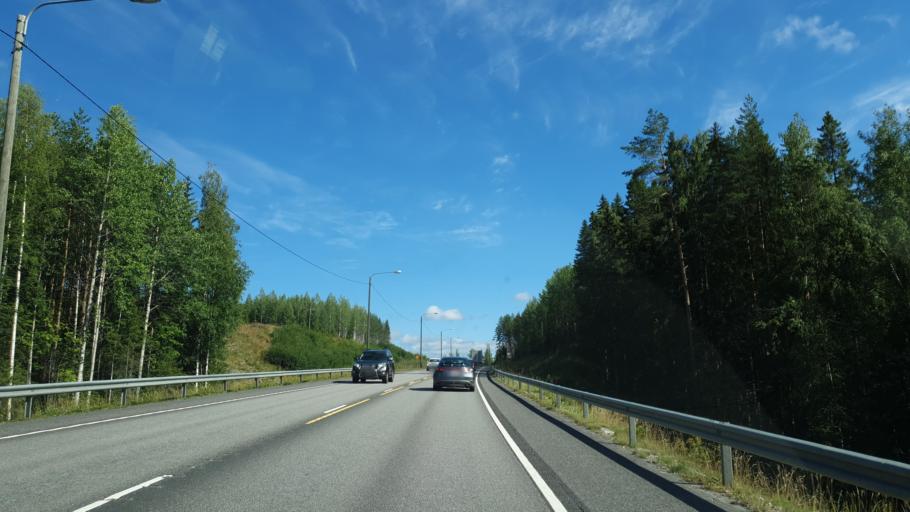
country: FI
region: Central Finland
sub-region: Jyvaeskylae
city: Toivakka
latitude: 62.2478
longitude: 26.0301
